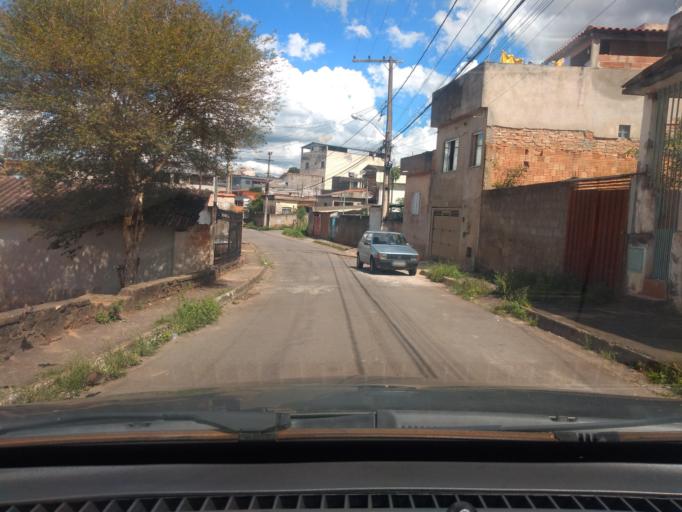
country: BR
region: Minas Gerais
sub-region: Tres Coracoes
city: Tres Coracoes
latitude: -21.6924
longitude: -45.2449
